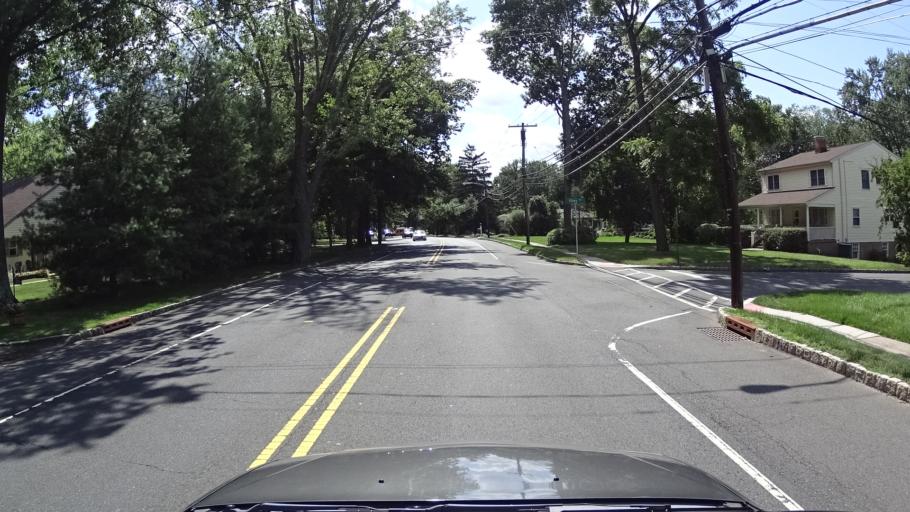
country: US
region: New Jersey
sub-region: Union County
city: New Providence
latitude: 40.7086
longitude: -74.3968
